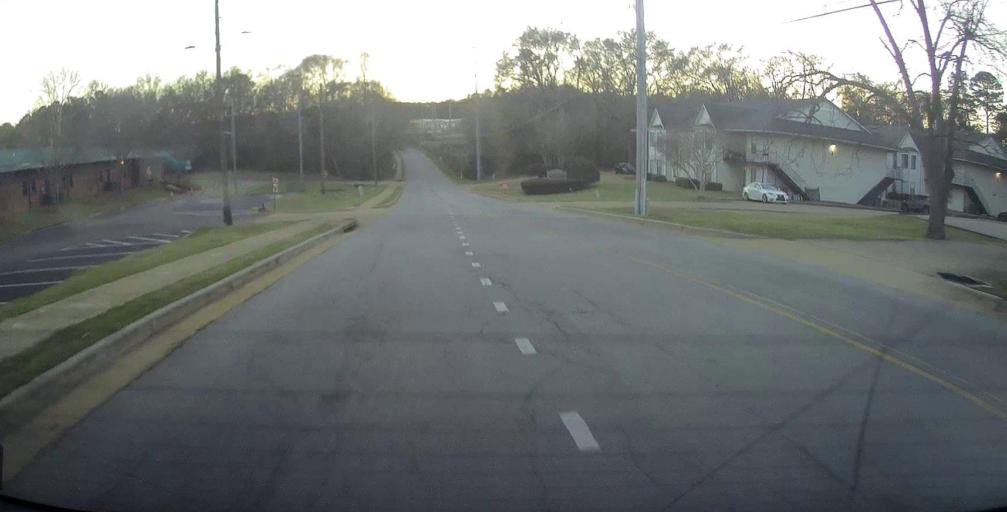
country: US
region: Alabama
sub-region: Russell County
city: Phenix City
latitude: 32.4846
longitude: -85.0269
